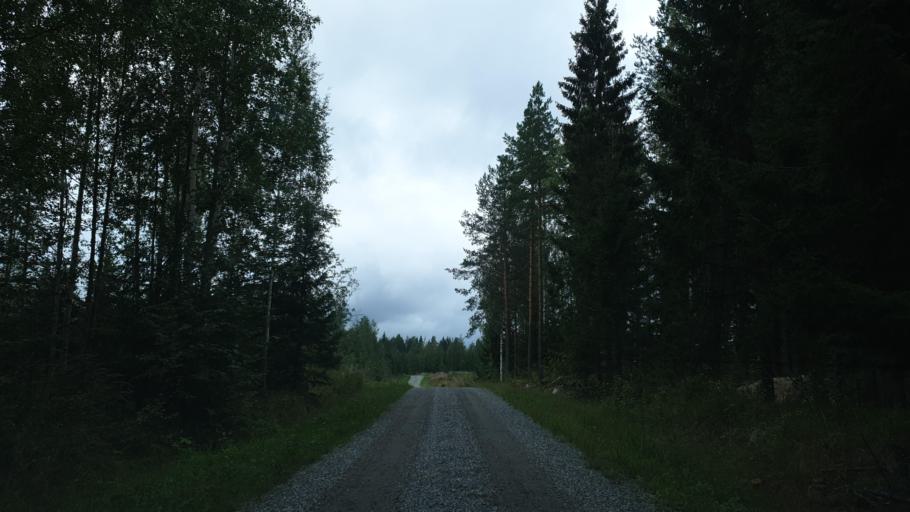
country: FI
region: Northern Savo
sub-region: Kuopio
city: Nilsiae
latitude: 63.2466
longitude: 28.2572
